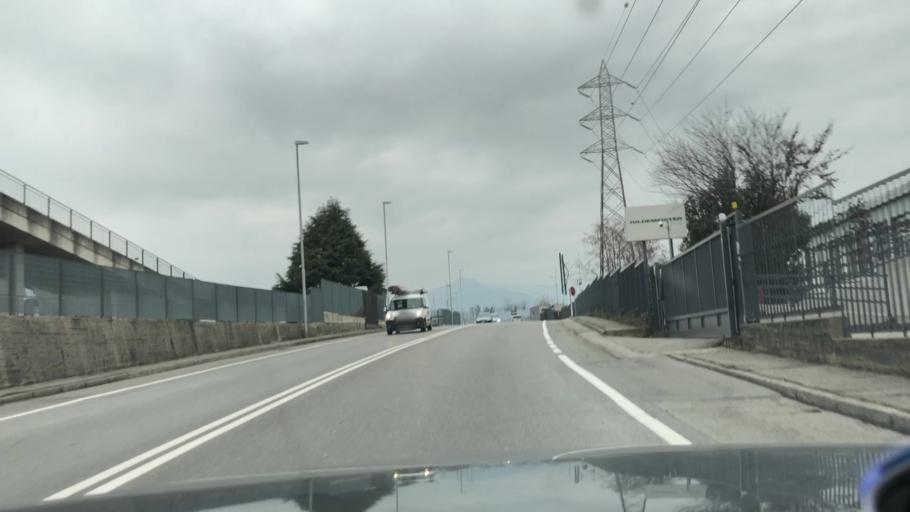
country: IT
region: Lombardy
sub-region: Provincia di Bergamo
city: Ponte San Pietro
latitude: 45.7054
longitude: 9.5835
